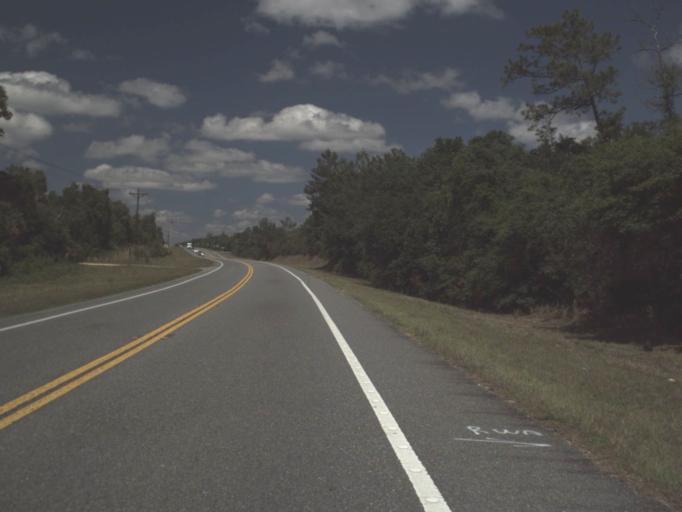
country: US
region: Florida
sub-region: Lake County
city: Astor
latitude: 29.1782
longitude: -81.7078
